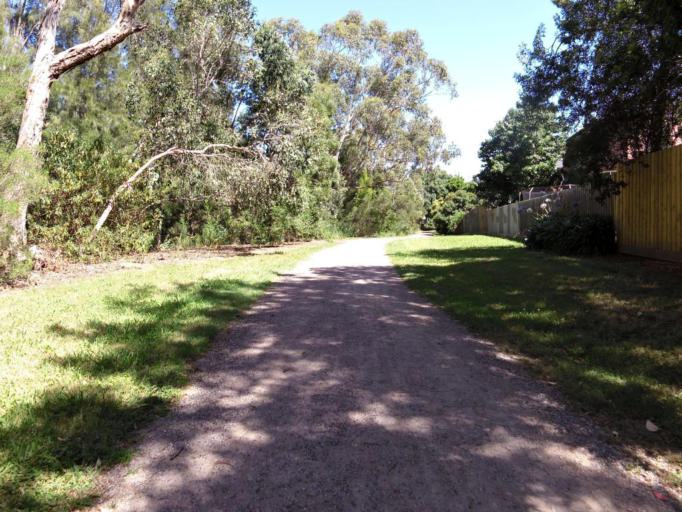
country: AU
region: Victoria
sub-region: Maroondah
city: Croydon North
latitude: -37.7808
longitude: 145.3059
